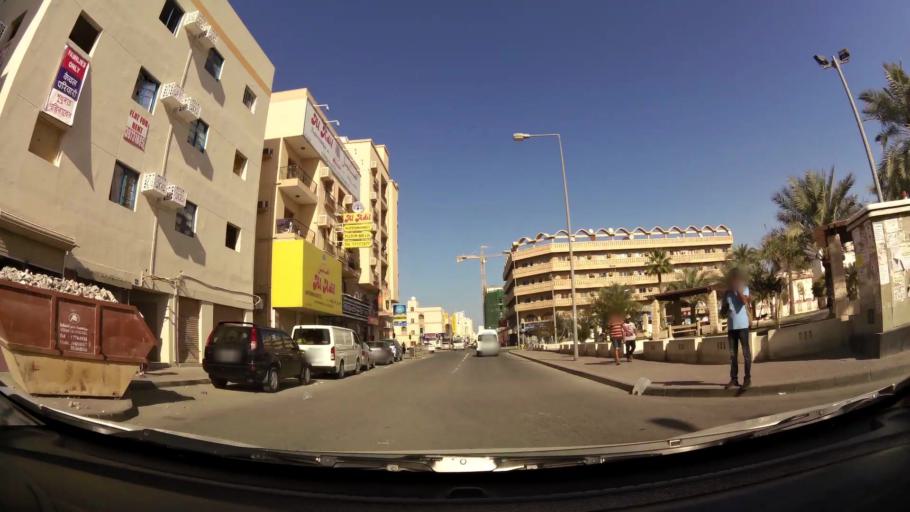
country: BH
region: Manama
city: Manama
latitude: 26.2278
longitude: 50.5816
